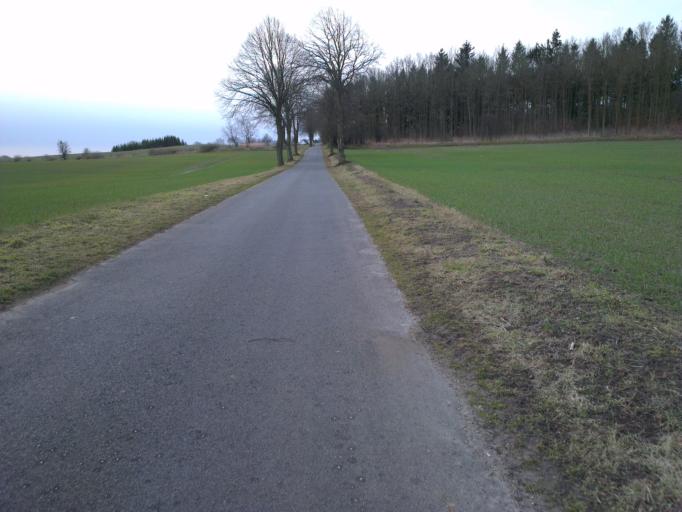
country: DK
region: Capital Region
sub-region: Frederikssund Kommune
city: Skibby
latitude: 55.7921
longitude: 11.9608
